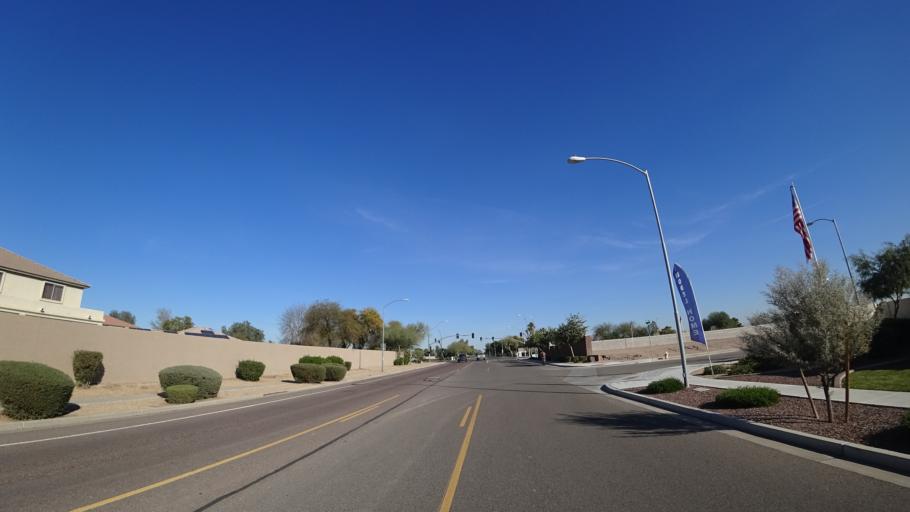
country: US
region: Arizona
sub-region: Maricopa County
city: Glendale
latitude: 33.5160
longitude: -112.2389
